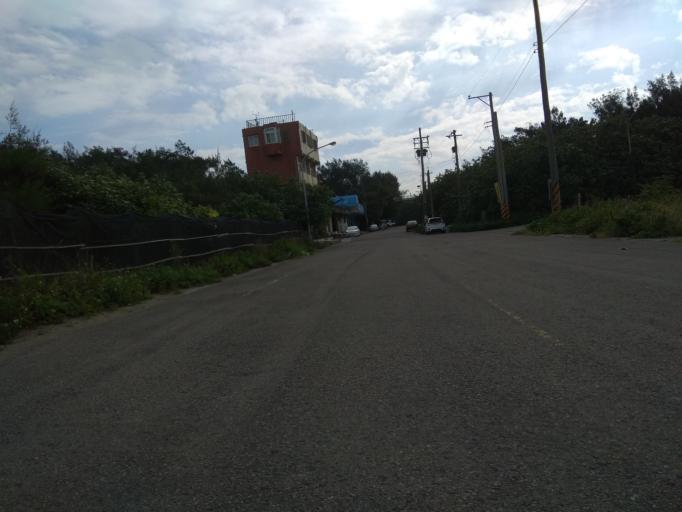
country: TW
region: Taiwan
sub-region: Hsinchu
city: Zhubei
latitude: 24.9264
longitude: 120.9736
